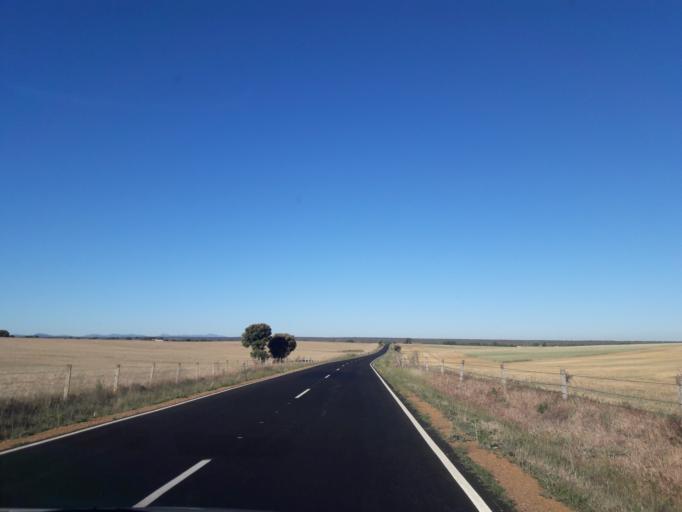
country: ES
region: Castille and Leon
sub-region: Provincia de Salamanca
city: Doninos de Salamanca
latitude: 40.9150
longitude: -5.7576
